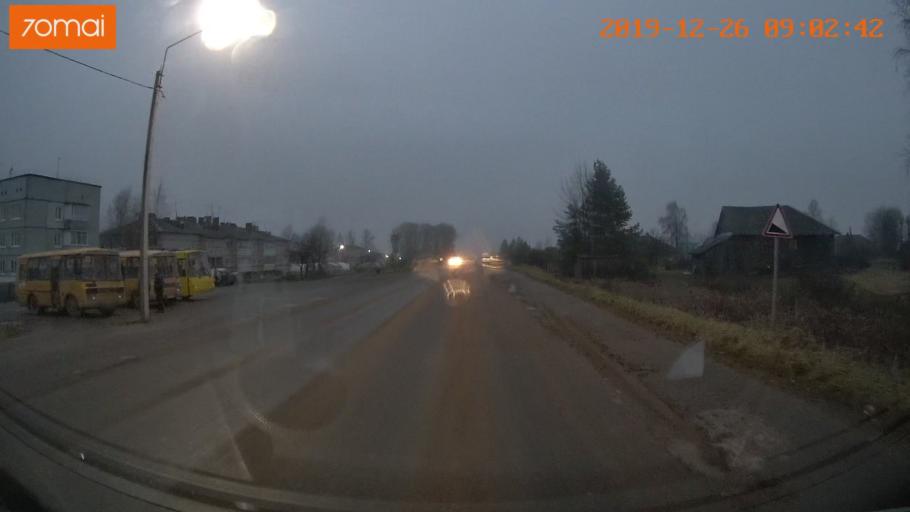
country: RU
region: Vologda
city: Gryazovets
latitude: 58.7973
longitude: 40.2660
